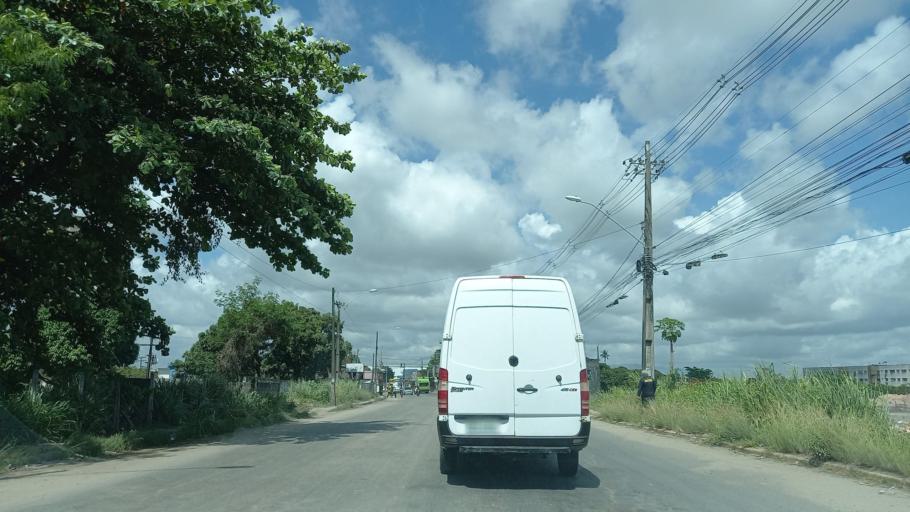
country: BR
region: Pernambuco
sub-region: Jaboatao Dos Guararapes
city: Jaboatao
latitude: -8.1539
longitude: -34.9542
